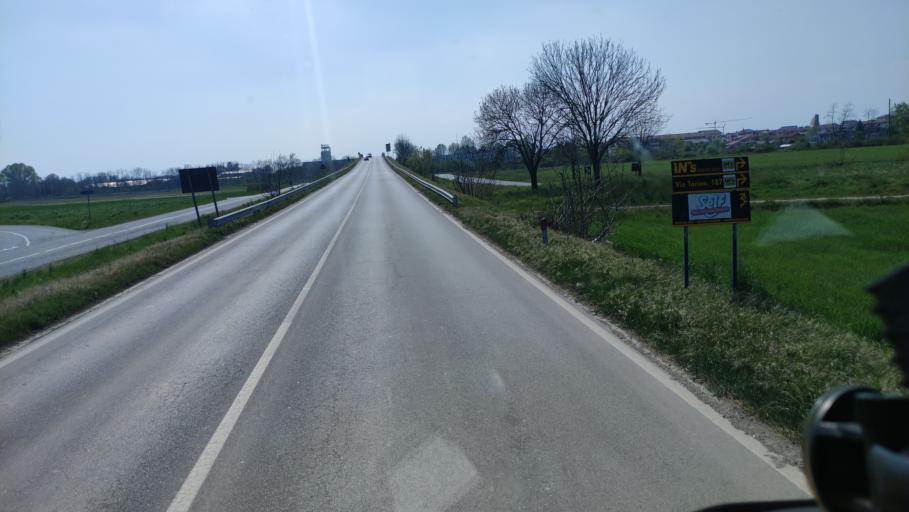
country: IT
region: Piedmont
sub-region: Provincia di Cuneo
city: Savigliano
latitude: 44.6402
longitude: 7.6704
